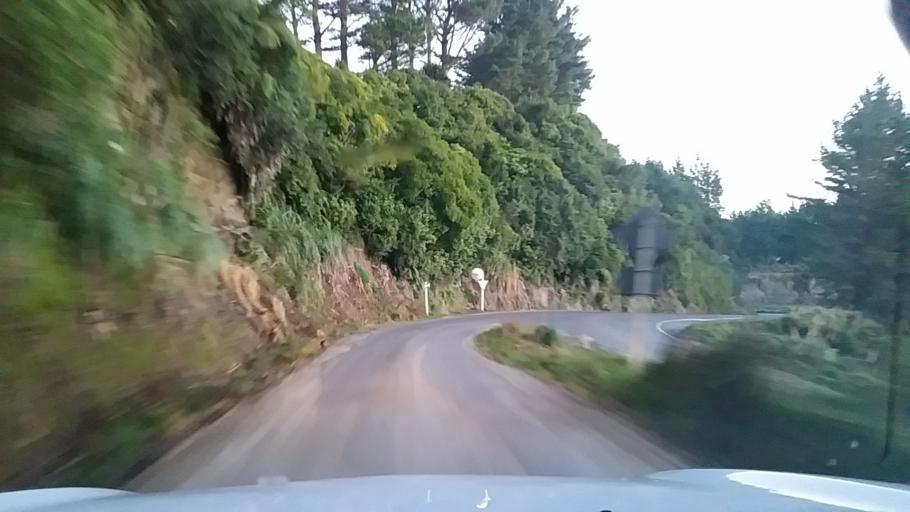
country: NZ
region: Manawatu-Wanganui
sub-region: Wanganui District
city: Wanganui
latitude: -39.7754
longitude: 174.8589
